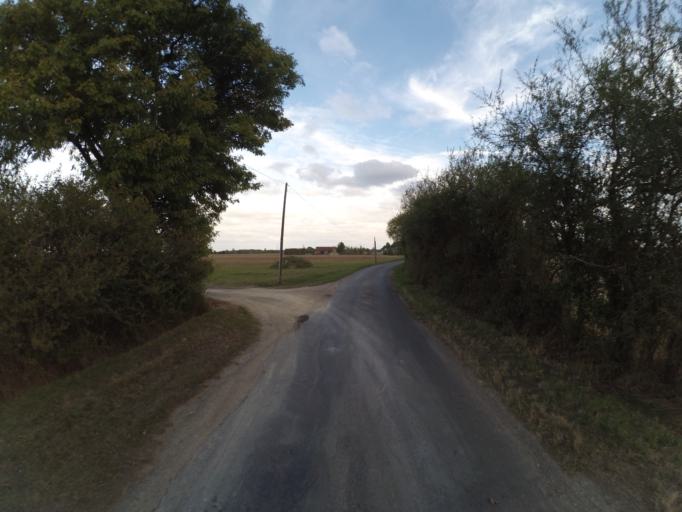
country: FR
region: Centre
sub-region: Departement d'Indre-et-Loire
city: Nazelles-Negron
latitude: 47.4474
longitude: 0.9605
